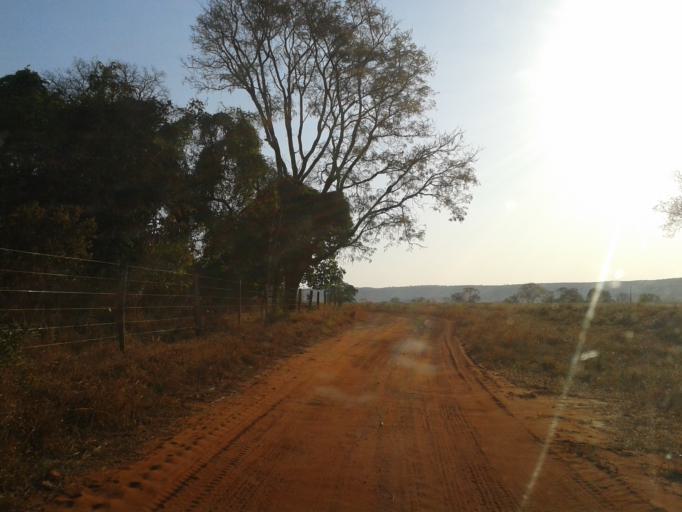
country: BR
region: Minas Gerais
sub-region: Ituiutaba
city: Ituiutaba
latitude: -19.2433
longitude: -49.5953
